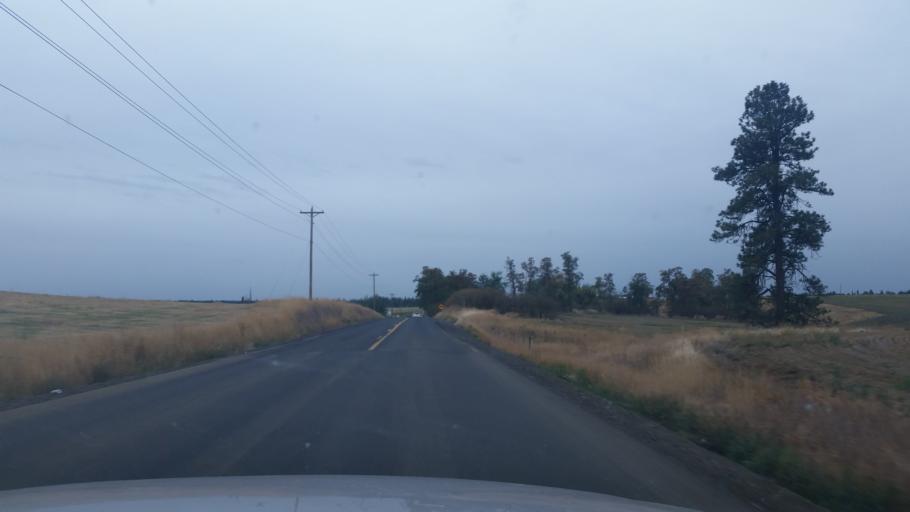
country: US
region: Washington
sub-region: Spokane County
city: Cheney
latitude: 47.5244
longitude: -117.5505
